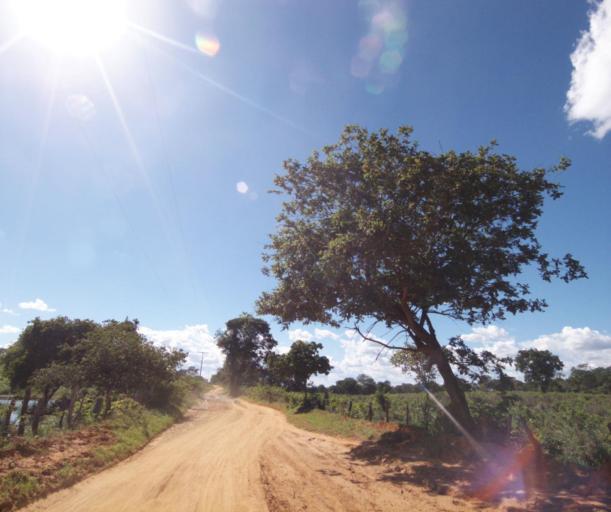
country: BR
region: Bahia
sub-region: Carinhanha
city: Carinhanha
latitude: -14.1826
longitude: -44.5060
